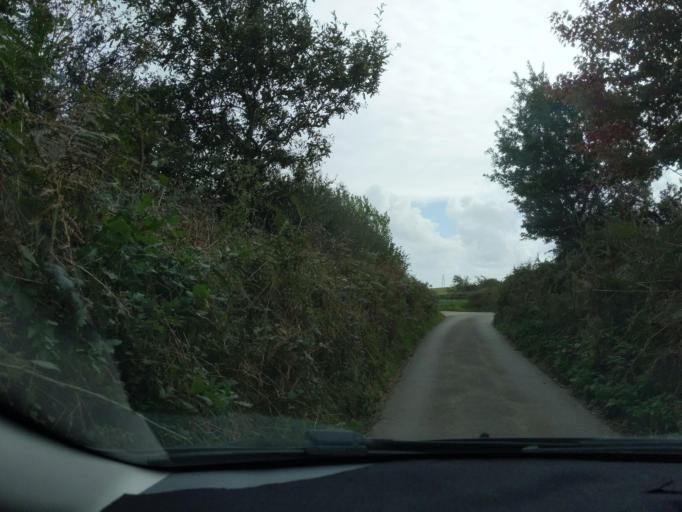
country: GB
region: England
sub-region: Cornwall
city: Lostwithiel
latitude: 50.3918
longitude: -4.7042
